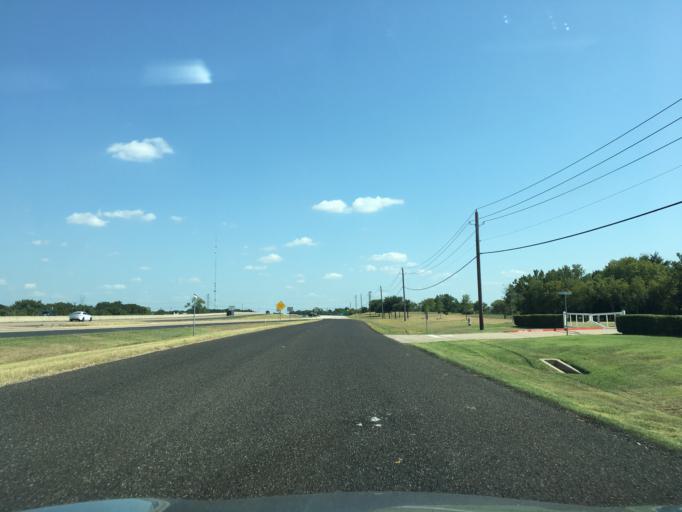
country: US
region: Texas
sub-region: Tarrant County
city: Kennedale
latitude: 32.6370
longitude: -97.1795
